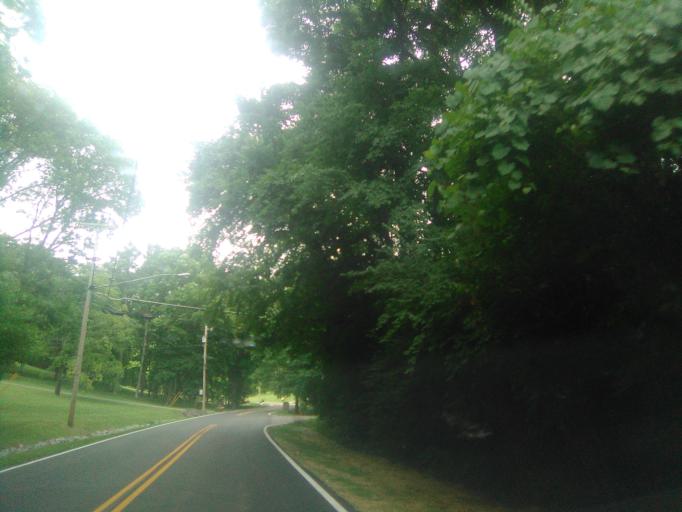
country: US
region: Tennessee
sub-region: Davidson County
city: Forest Hills
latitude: 36.0647
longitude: -86.8557
